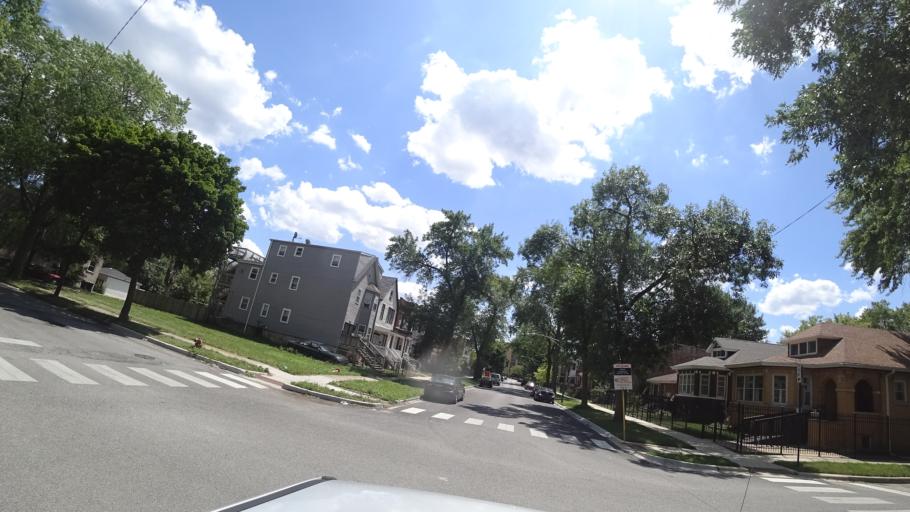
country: US
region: Illinois
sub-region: Cook County
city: Chicago
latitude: 41.7713
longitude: -87.6082
